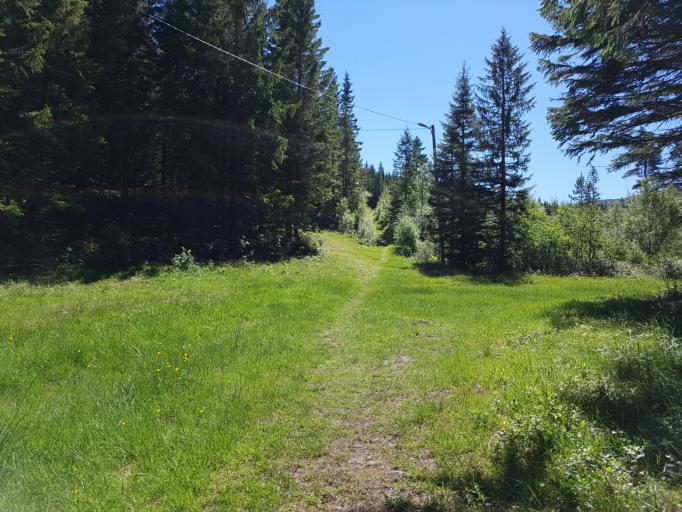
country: NO
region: Sor-Trondelag
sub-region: Skaun
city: Borsa
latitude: 63.4338
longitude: 10.1926
